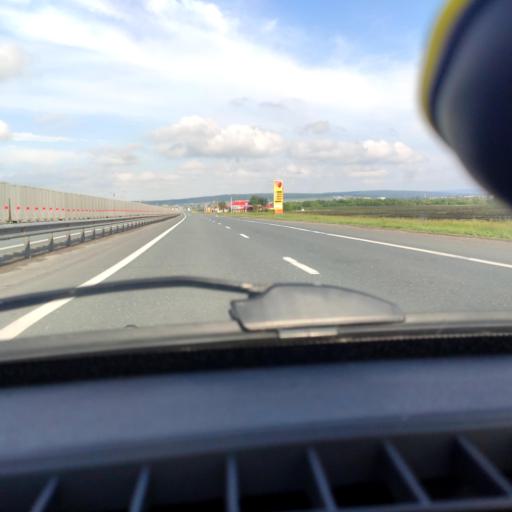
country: RU
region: Samara
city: Kurumoch
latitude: 53.5031
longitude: 49.9924
